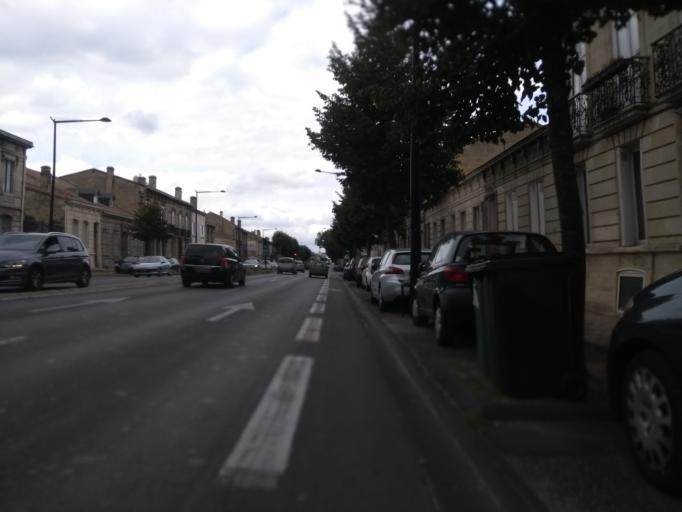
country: FR
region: Aquitaine
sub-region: Departement de la Gironde
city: Talence
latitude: 44.8177
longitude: -0.5772
